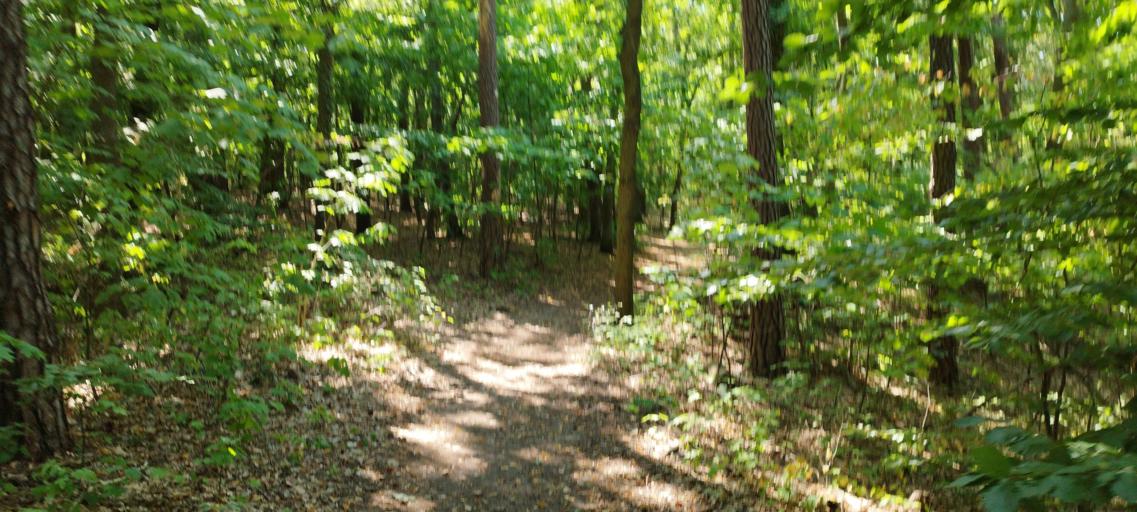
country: DE
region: Brandenburg
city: Rehfelde
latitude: 52.5310
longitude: 13.8463
